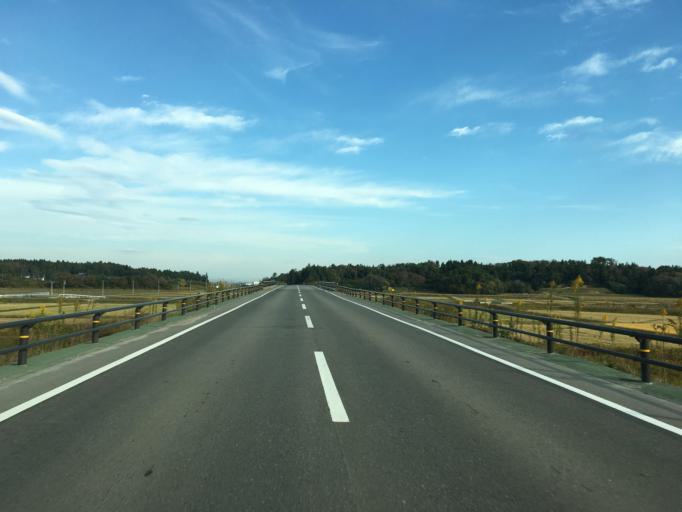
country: JP
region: Miyagi
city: Marumori
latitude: 37.8892
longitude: 140.9258
